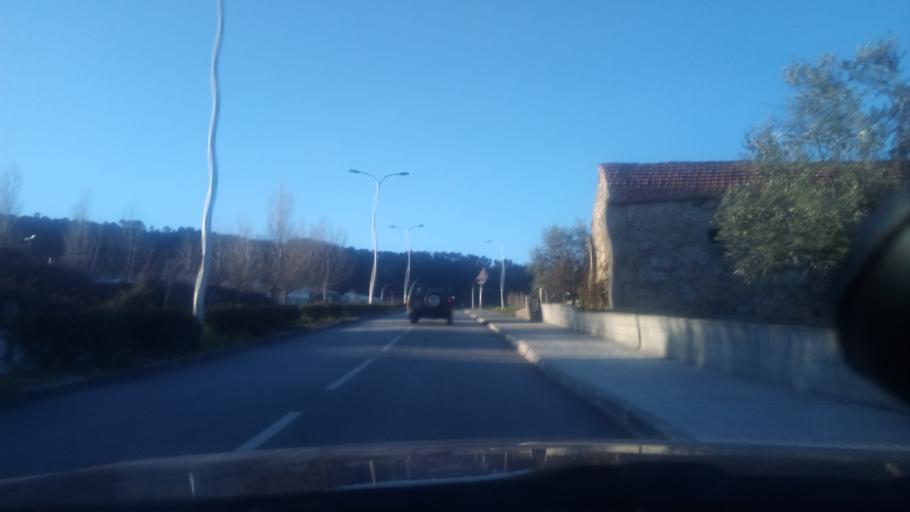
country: PT
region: Guarda
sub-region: Fornos de Algodres
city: Fornos de Algodres
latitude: 40.6182
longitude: -7.5349
